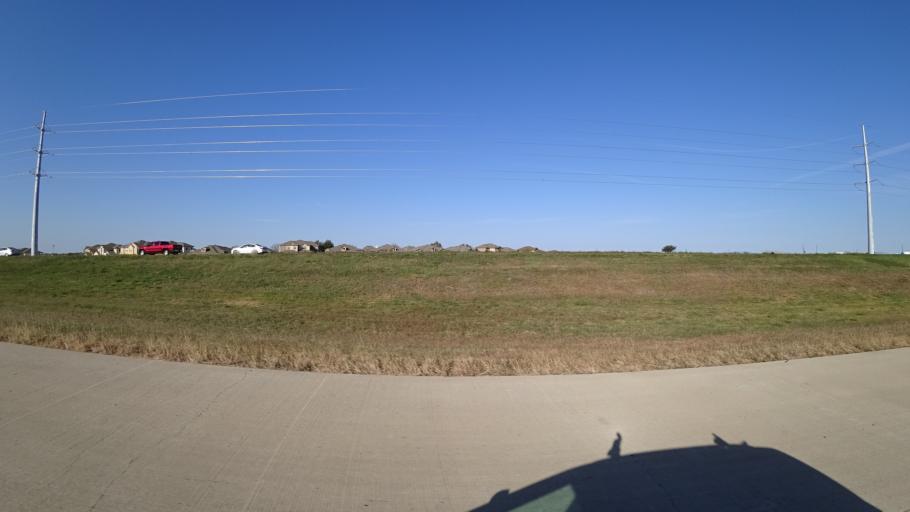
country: US
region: Texas
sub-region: Williamson County
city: Hutto
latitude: 30.4989
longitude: -97.5821
